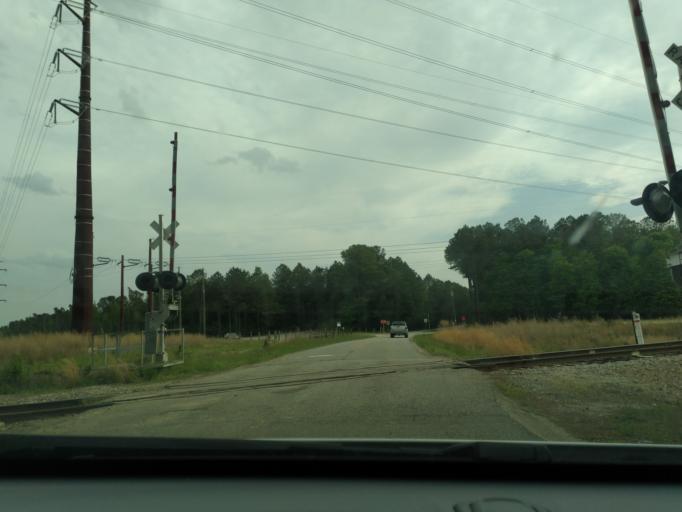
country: US
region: Virginia
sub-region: York County
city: Yorktown
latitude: 37.1733
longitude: -76.5151
